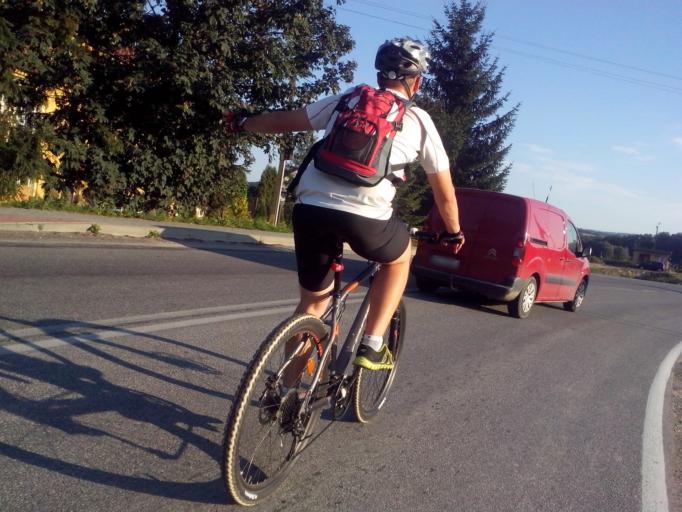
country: PL
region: Subcarpathian Voivodeship
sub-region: Powiat strzyzowski
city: Strzyzow
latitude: 49.8754
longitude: 21.8179
